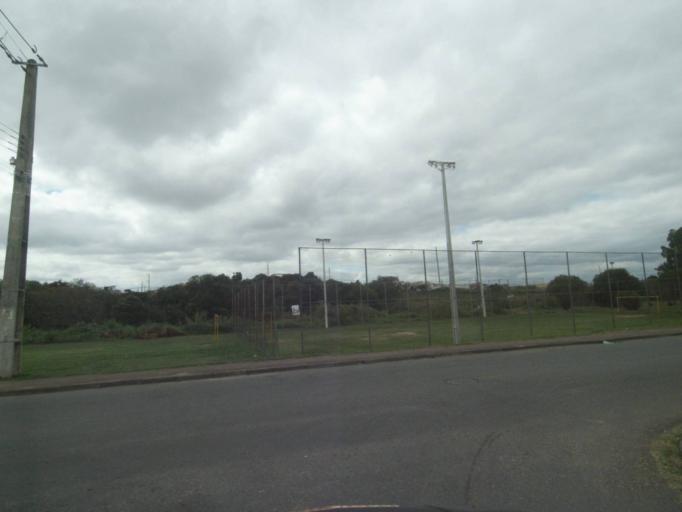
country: BR
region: Parana
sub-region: Sao Jose Dos Pinhais
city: Sao Jose dos Pinhais
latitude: -25.5535
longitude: -49.2585
